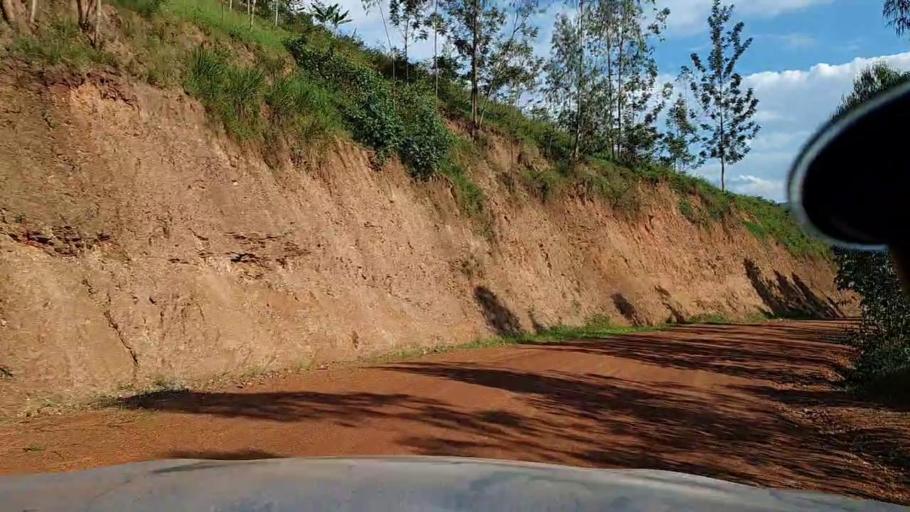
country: RW
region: Kigali
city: Kigali
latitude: -1.8469
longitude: 29.8625
